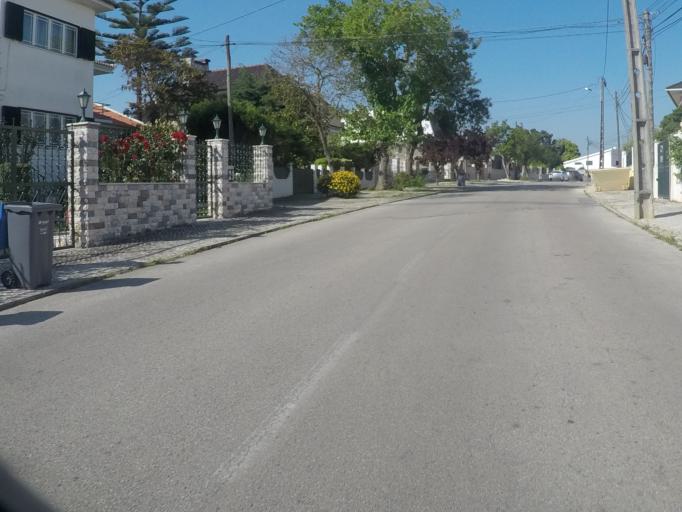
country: PT
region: Setubal
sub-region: Seixal
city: Amora
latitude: 38.5980
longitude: -9.1434
